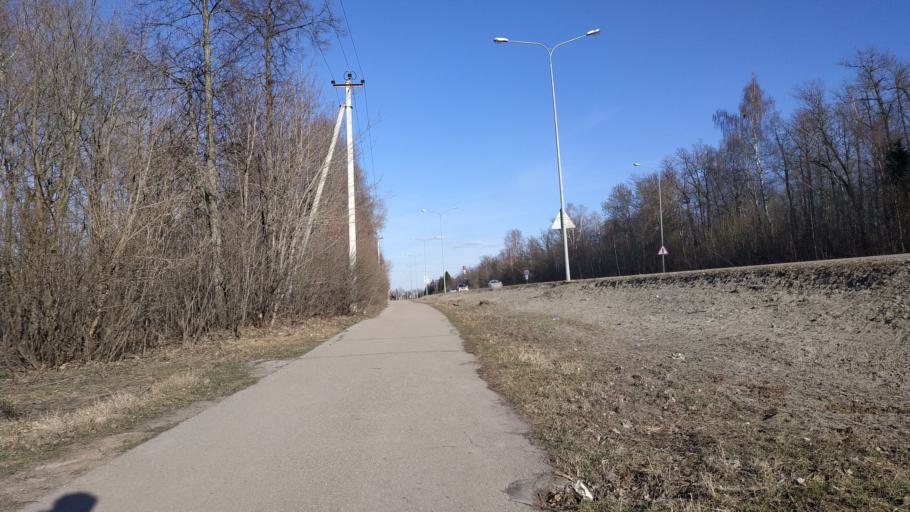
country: RU
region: Chuvashia
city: Novyye Lapsary
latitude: 56.1312
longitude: 47.1471
